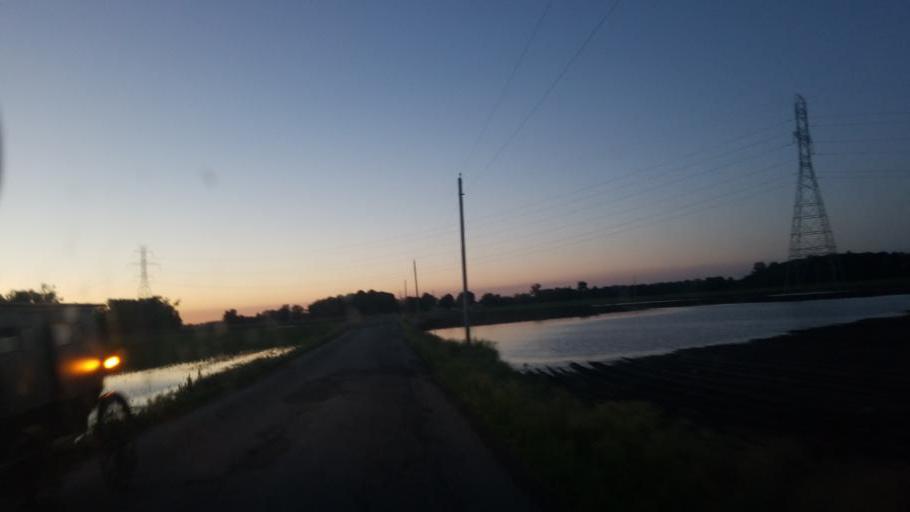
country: US
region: Indiana
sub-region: Marshall County
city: Bremen
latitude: 41.4696
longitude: -86.1177
